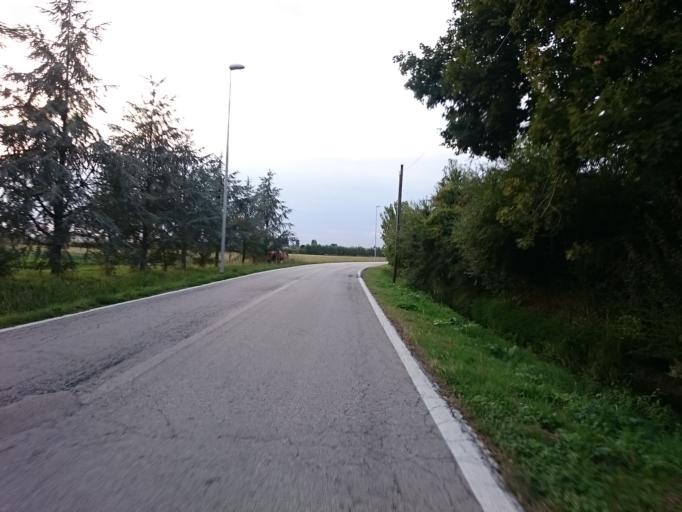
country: IT
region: Veneto
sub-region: Provincia di Vicenza
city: Grisignano di Zocco
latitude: 45.4900
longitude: 11.7150
